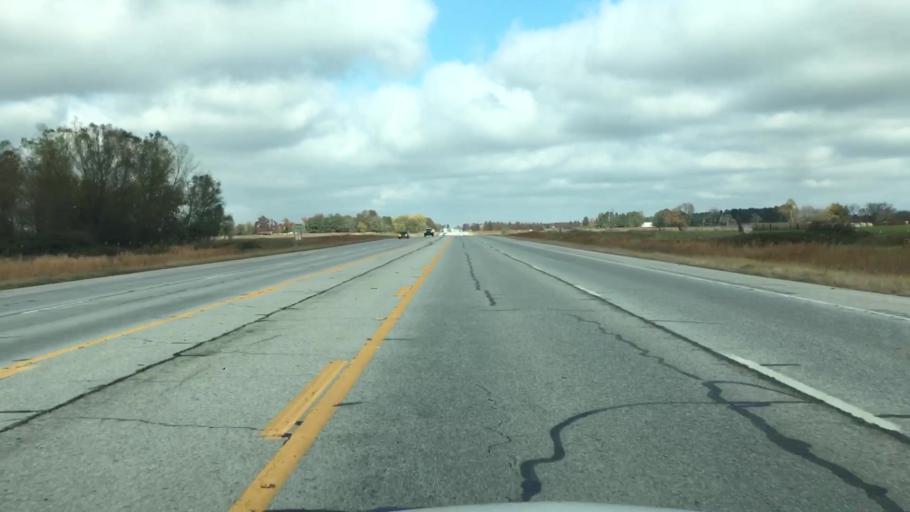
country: US
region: Arkansas
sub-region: Benton County
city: Siloam Springs
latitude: 36.1979
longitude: -94.4960
